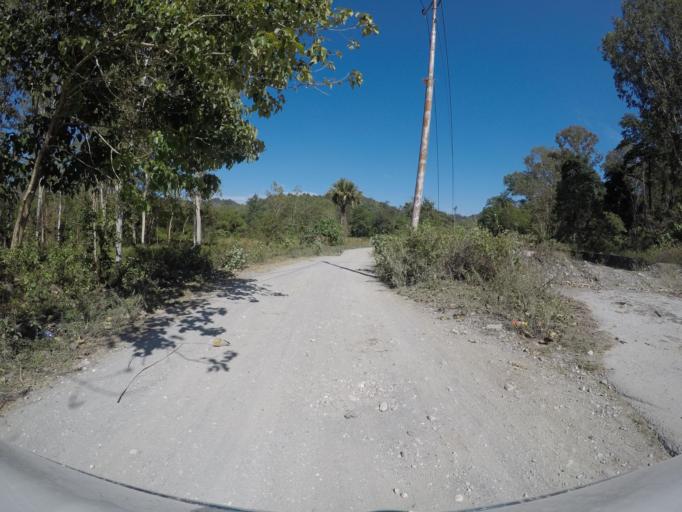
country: TL
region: Manufahi
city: Same
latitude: -8.9597
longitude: 126.0106
